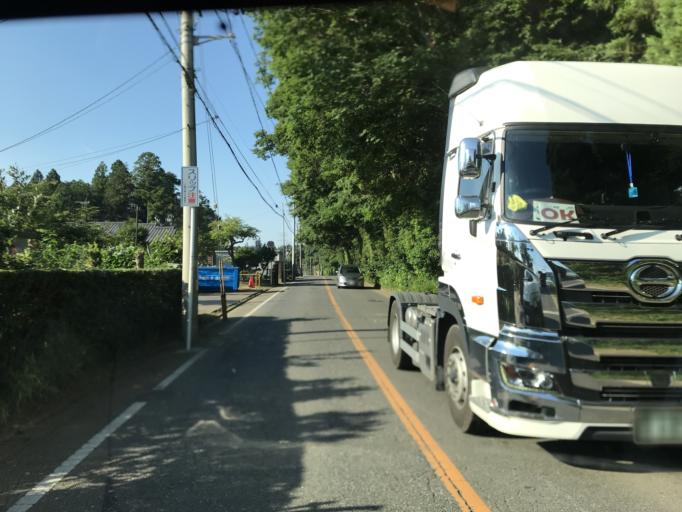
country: JP
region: Chiba
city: Chiba
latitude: 35.5693
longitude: 140.2049
